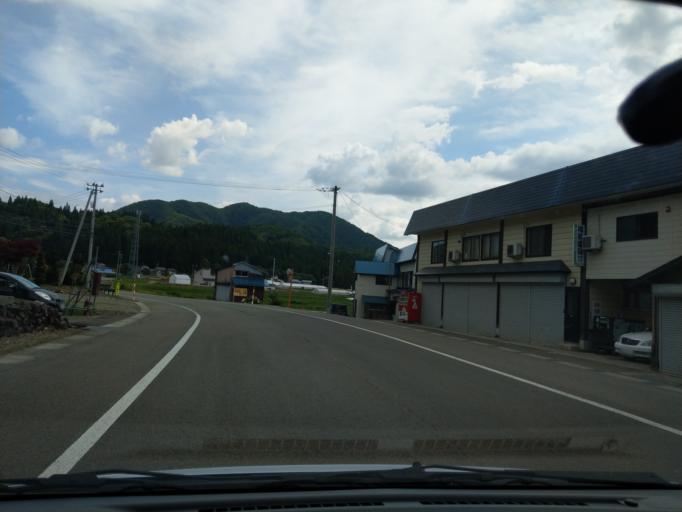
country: JP
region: Akita
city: Kakunodatemachi
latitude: 39.7034
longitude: 140.5848
